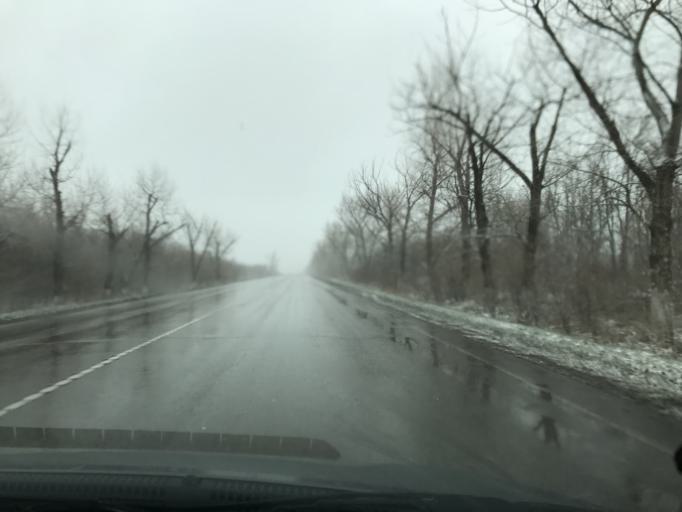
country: RU
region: Rostov
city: Kirovskaya
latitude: 47.0242
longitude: 39.8917
